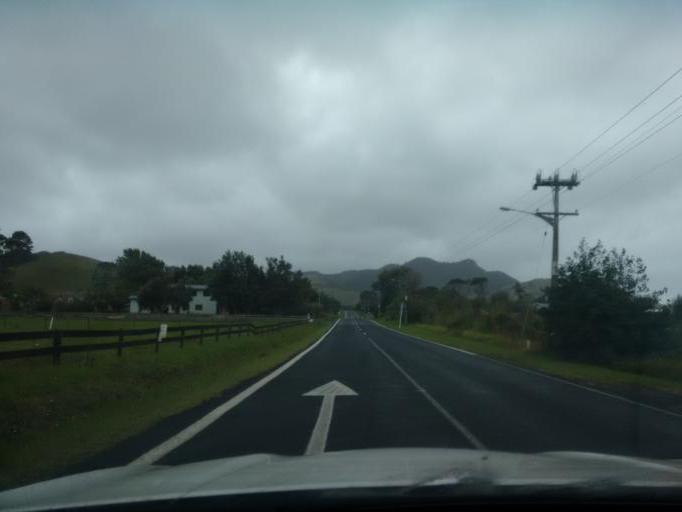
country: NZ
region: Waikato
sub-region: Thames-Coromandel District
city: Whitianga
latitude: -36.8018
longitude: 175.7192
